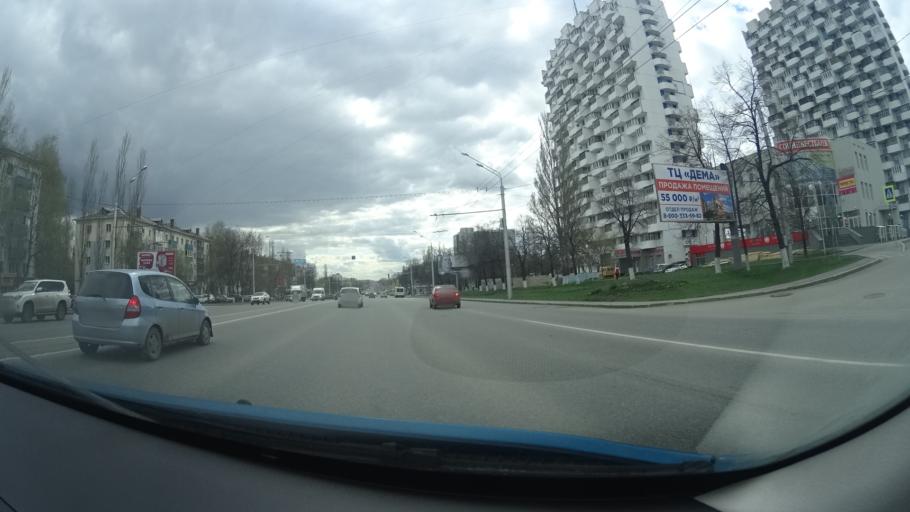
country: RU
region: Bashkortostan
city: Ufa
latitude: 54.7642
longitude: 56.0155
